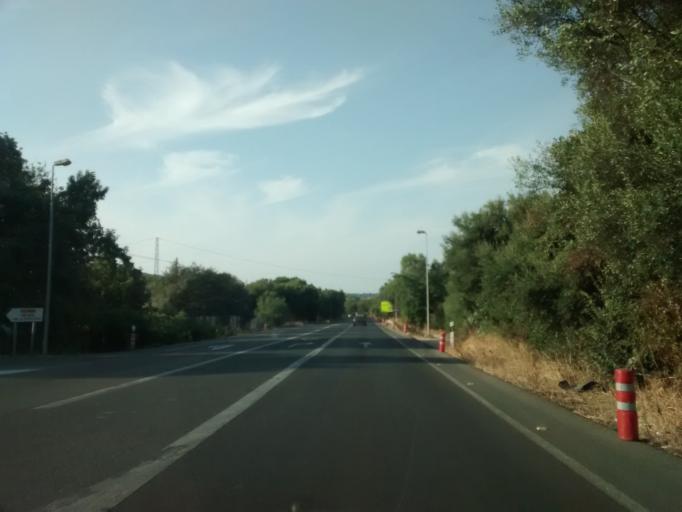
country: ES
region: Andalusia
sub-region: Provincia de Cadiz
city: Vejer de la Frontera
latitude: 36.2455
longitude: -5.9498
